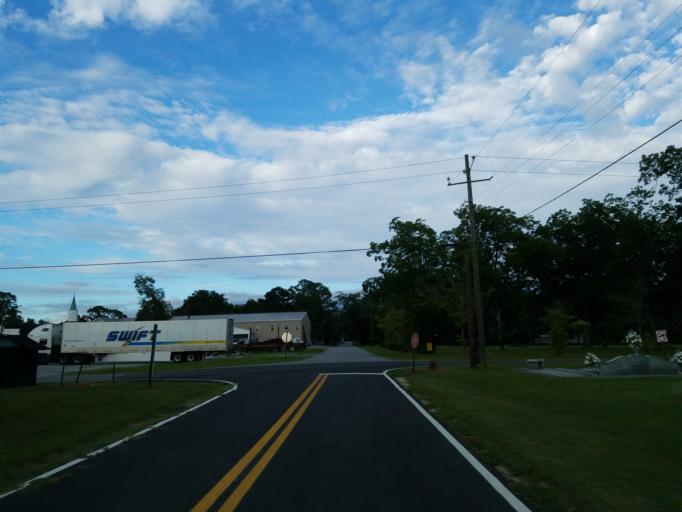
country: US
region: Georgia
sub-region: Cook County
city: Sparks
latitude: 31.2699
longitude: -83.4699
